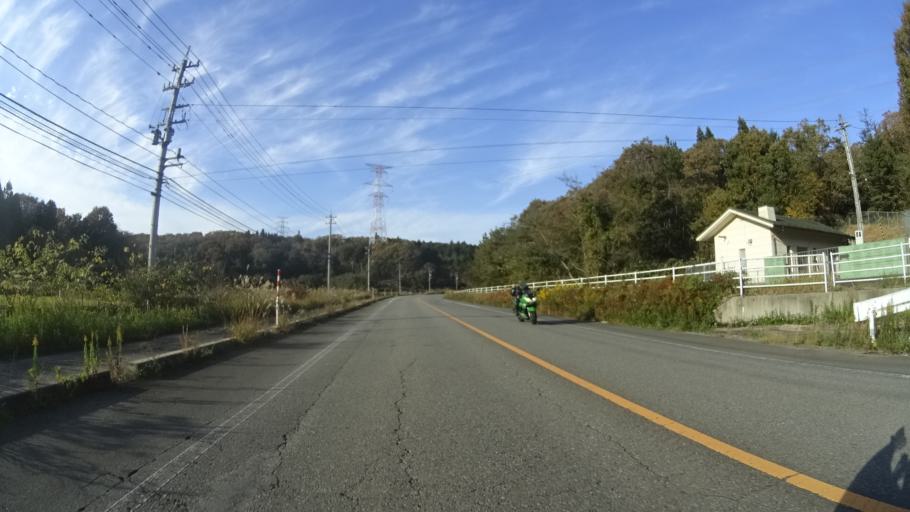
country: JP
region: Ishikawa
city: Hakui
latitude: 37.0464
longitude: 136.7748
